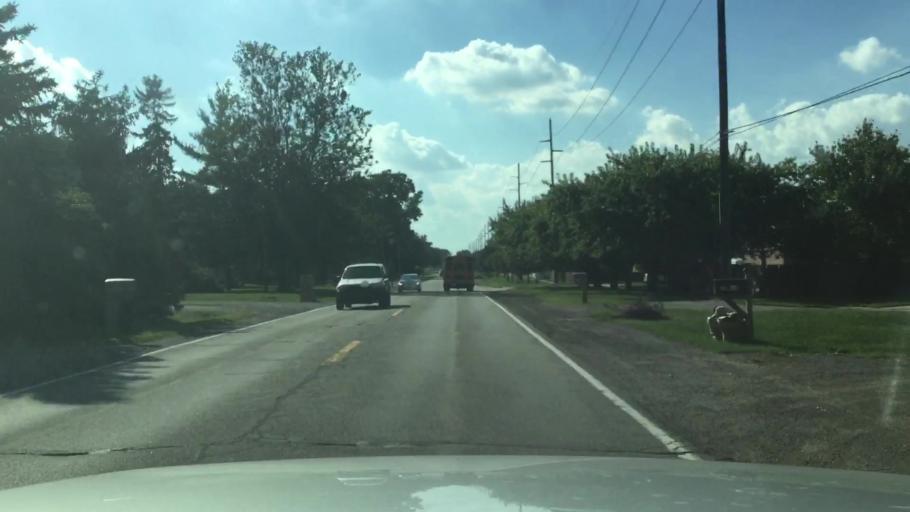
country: US
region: Michigan
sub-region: Wayne County
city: Westland
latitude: 42.3527
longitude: -83.4228
